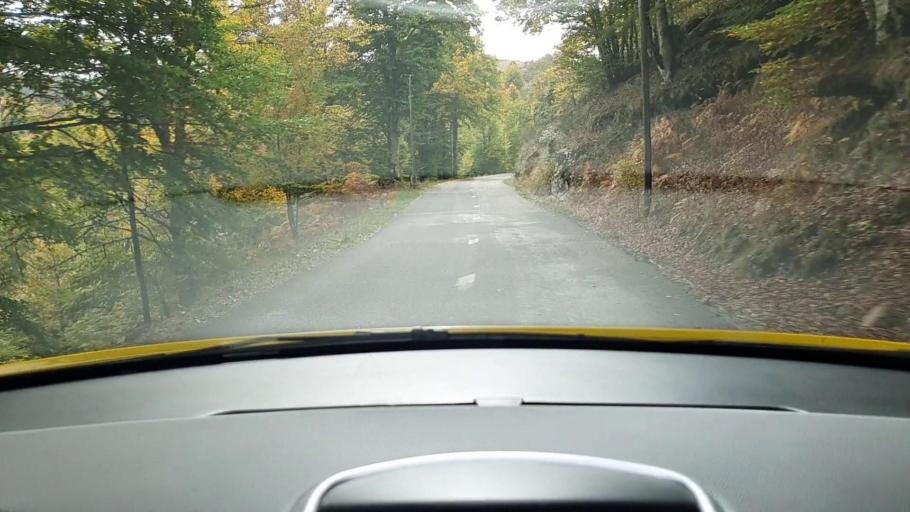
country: FR
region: Languedoc-Roussillon
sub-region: Departement du Gard
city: Le Vigan
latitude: 44.0738
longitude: 3.5225
